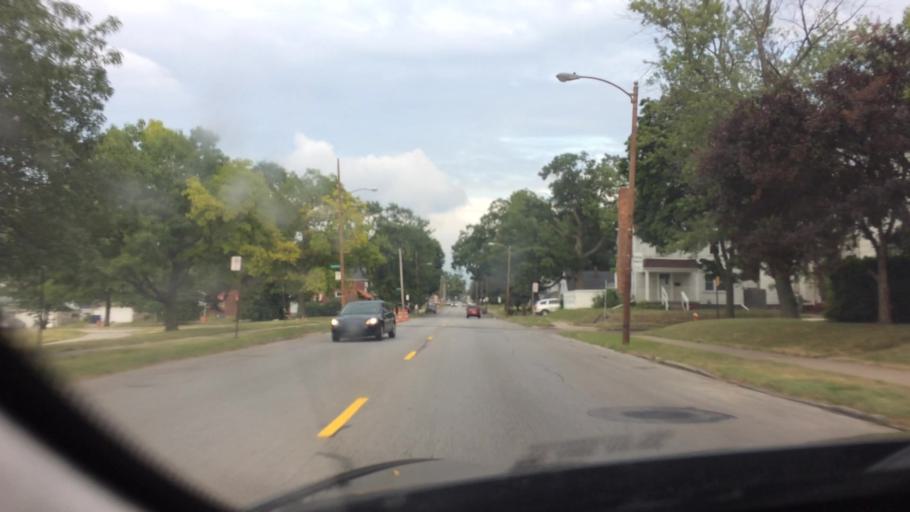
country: US
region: Ohio
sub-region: Wood County
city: Rossford
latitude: 41.6307
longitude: -83.5832
